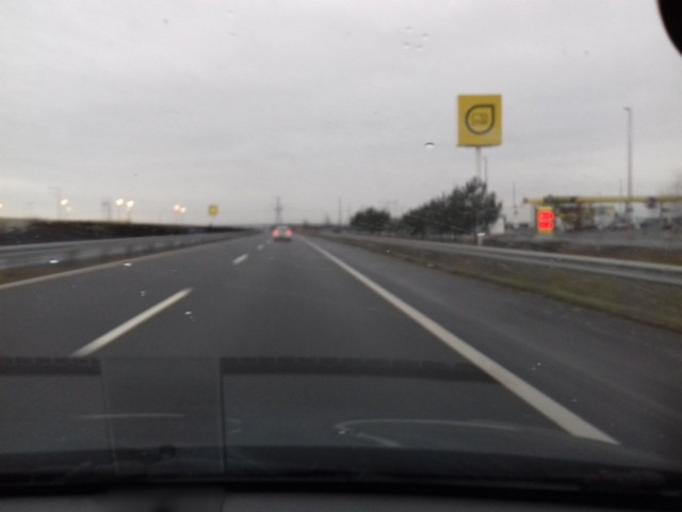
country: HU
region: Hajdu-Bihar
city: Hajduboszormeny
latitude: 47.6091
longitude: 21.5209
